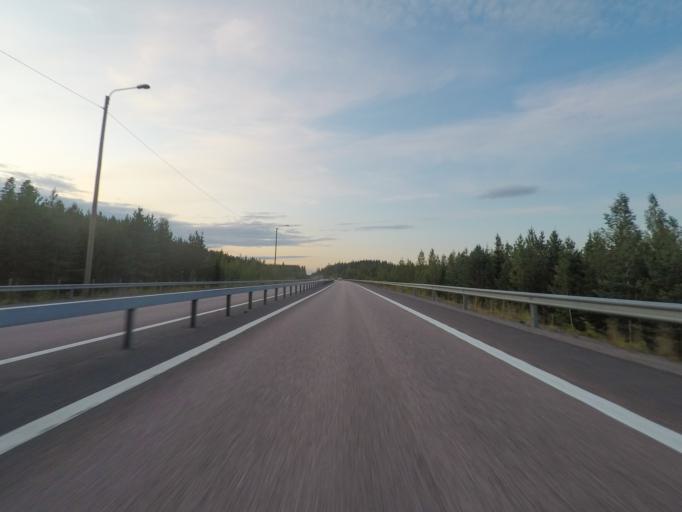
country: FI
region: Central Finland
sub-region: Jyvaeskylae
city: Saeynaetsalo
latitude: 62.1743
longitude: 25.9064
